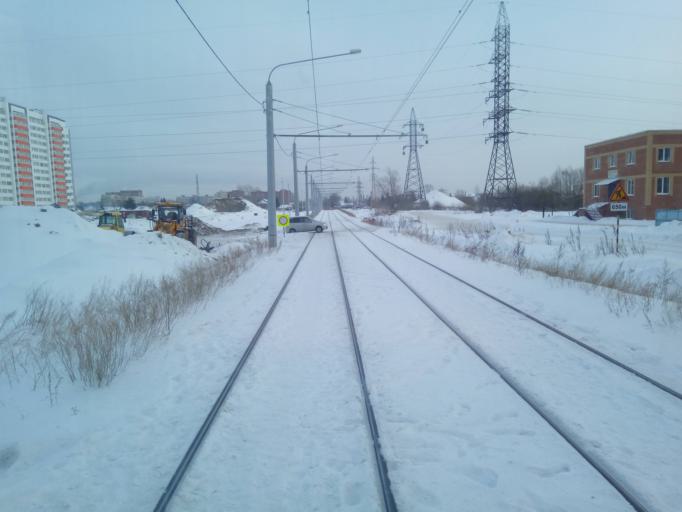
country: RU
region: Novosibirsk
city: Tolmachevo
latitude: 54.9791
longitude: 82.8118
